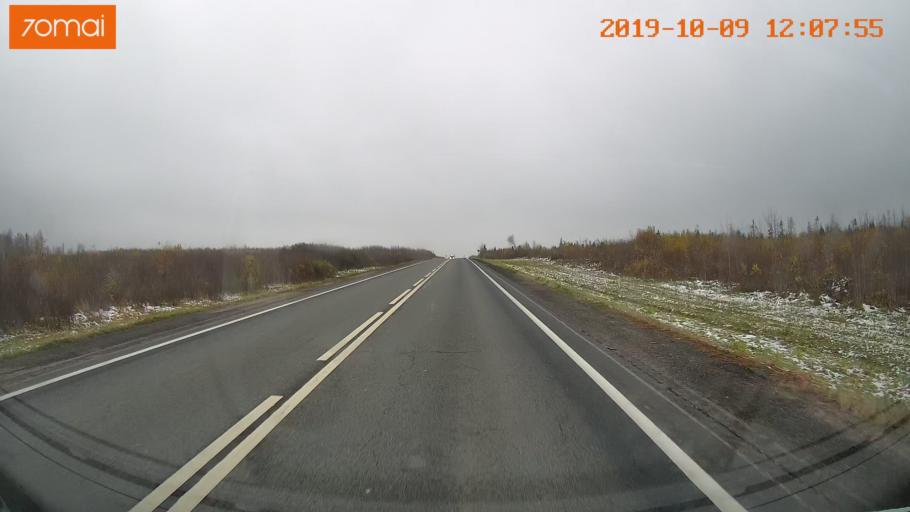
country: RU
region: Jaroslavl
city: Prechistoye
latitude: 58.5933
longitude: 40.3447
